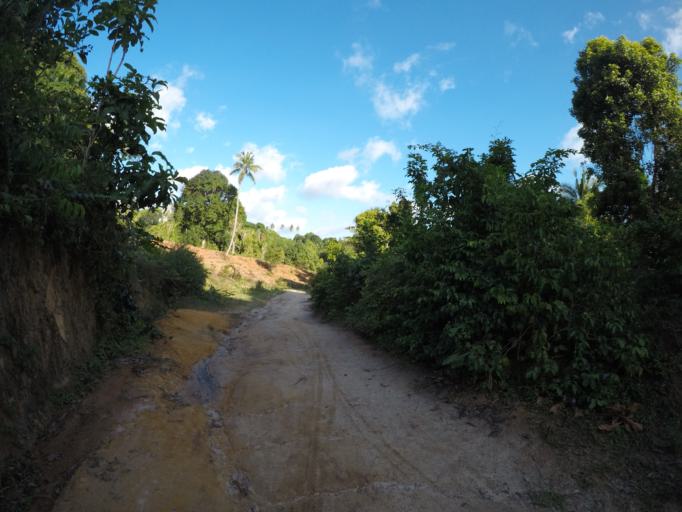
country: TZ
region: Pemba South
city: Mtambile
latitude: -5.3870
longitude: 39.7363
